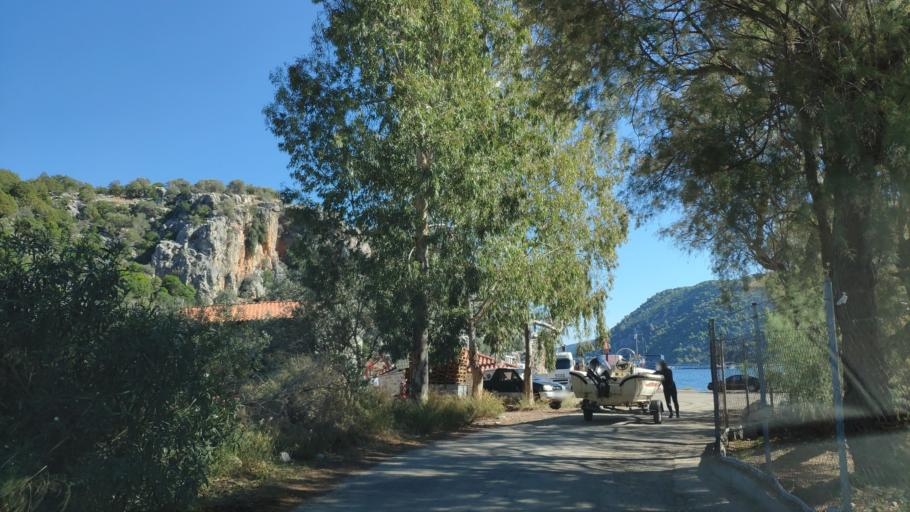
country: GR
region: Peloponnese
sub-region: Nomos Korinthias
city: Sofikon
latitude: 37.7333
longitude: 23.1177
